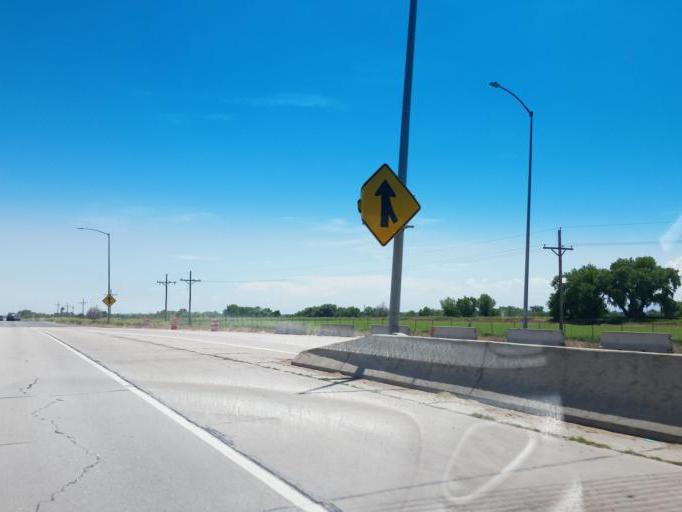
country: US
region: Colorado
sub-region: Larimer County
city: Fort Collins
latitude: 40.5558
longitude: -105.0008
